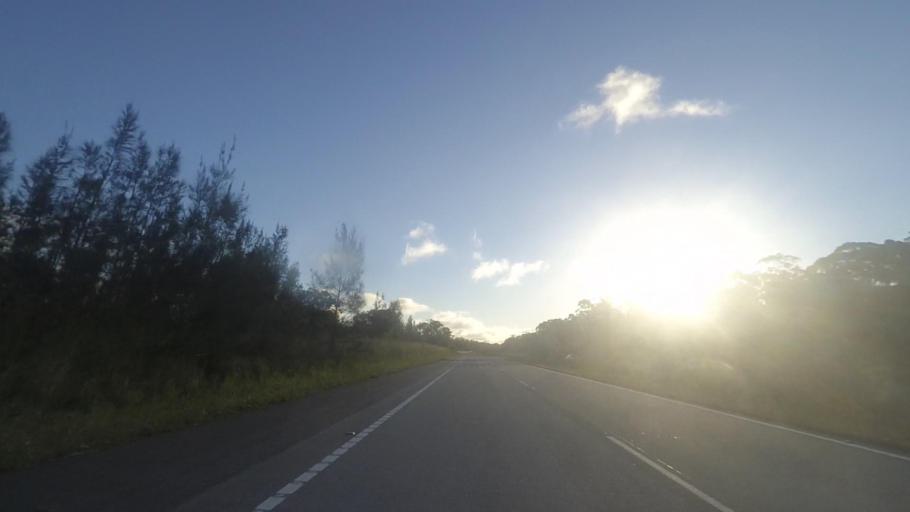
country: AU
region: New South Wales
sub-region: Great Lakes
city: Hawks Nest
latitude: -32.5419
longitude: 152.1660
